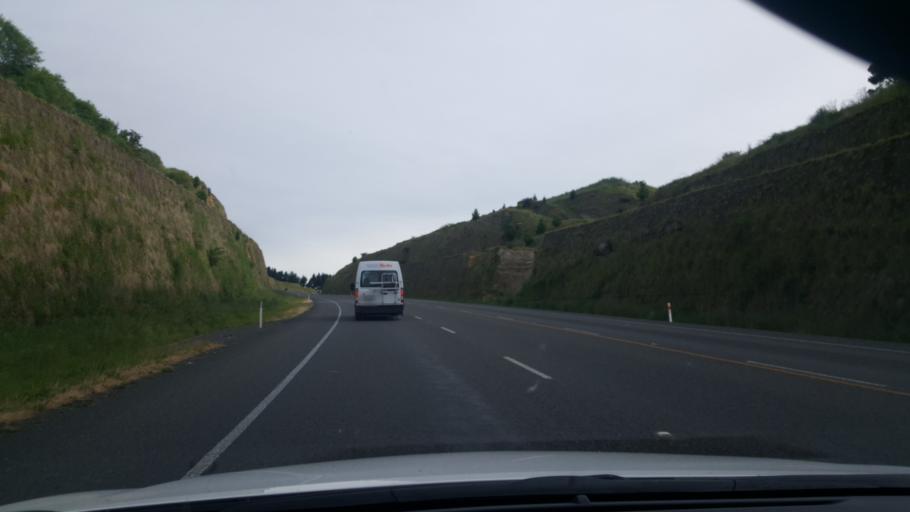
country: NZ
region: Waikato
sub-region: Taupo District
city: Taupo
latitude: -38.6381
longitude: 176.0975
